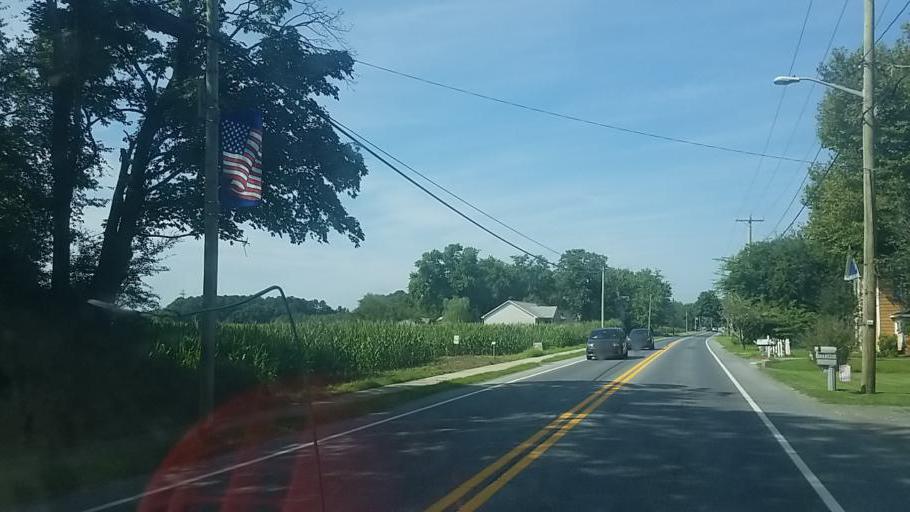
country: US
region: Delaware
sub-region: Sussex County
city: Millsboro
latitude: 38.5465
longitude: -75.2510
